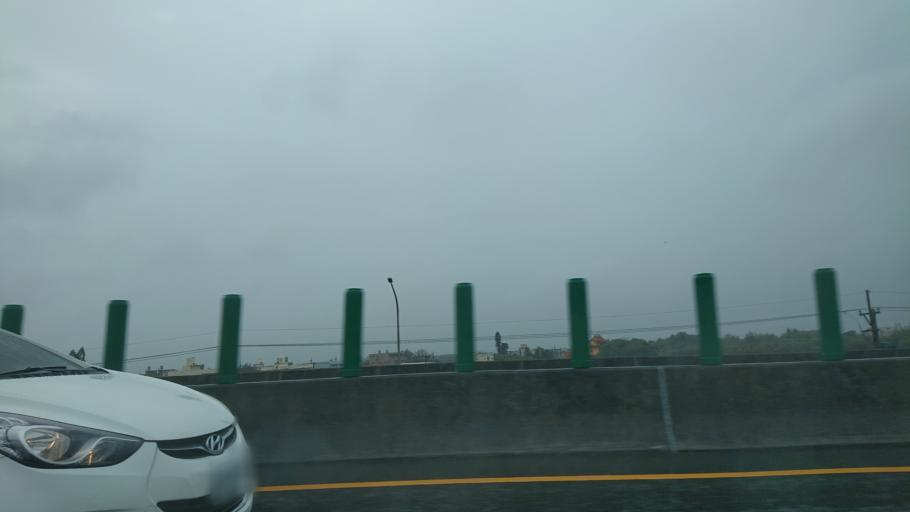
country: TW
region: Taiwan
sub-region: Chiayi
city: Taibao
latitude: 23.7364
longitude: 120.2366
